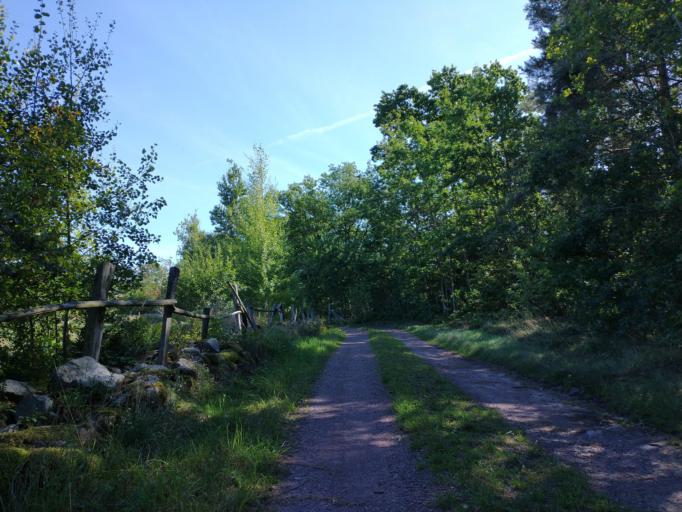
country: SE
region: Kalmar
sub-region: Kalmar Kommun
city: Lindsdal
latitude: 56.7853
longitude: 16.2871
